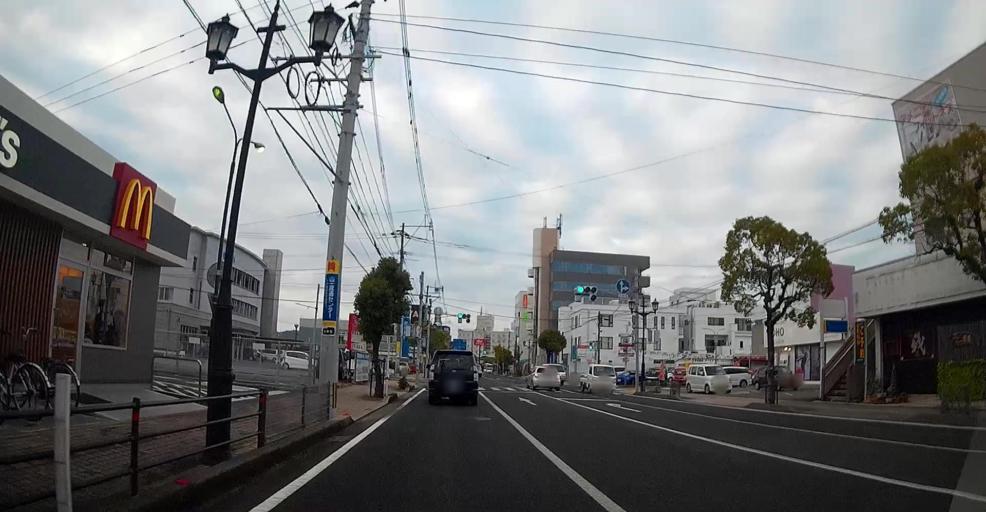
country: JP
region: Kumamoto
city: Hondo
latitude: 32.4530
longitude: 130.1954
